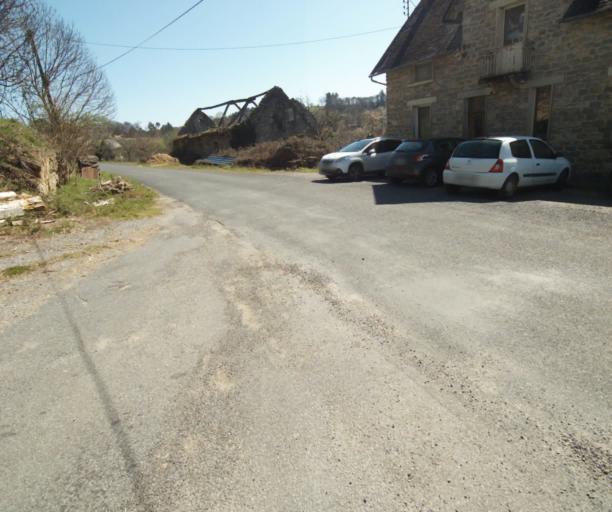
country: FR
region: Limousin
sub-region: Departement de la Correze
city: Saint-Mexant
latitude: 45.2874
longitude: 1.6365
